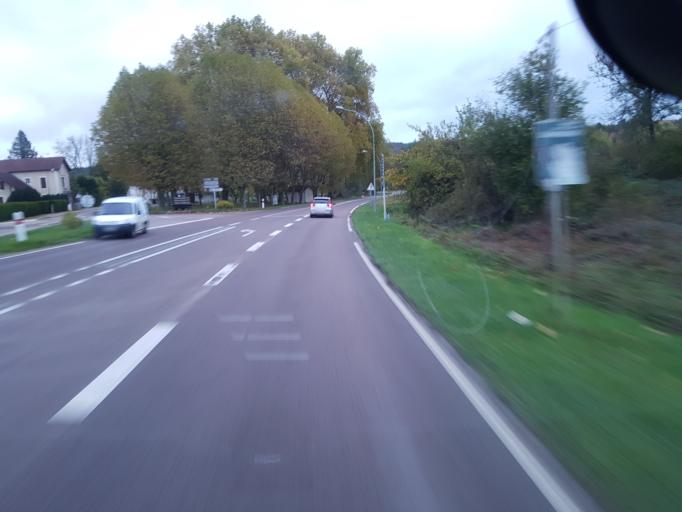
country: FR
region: Champagne-Ardenne
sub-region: Departement de l'Aube
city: Mussy-sur-Seine
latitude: 47.9746
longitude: 4.5003
